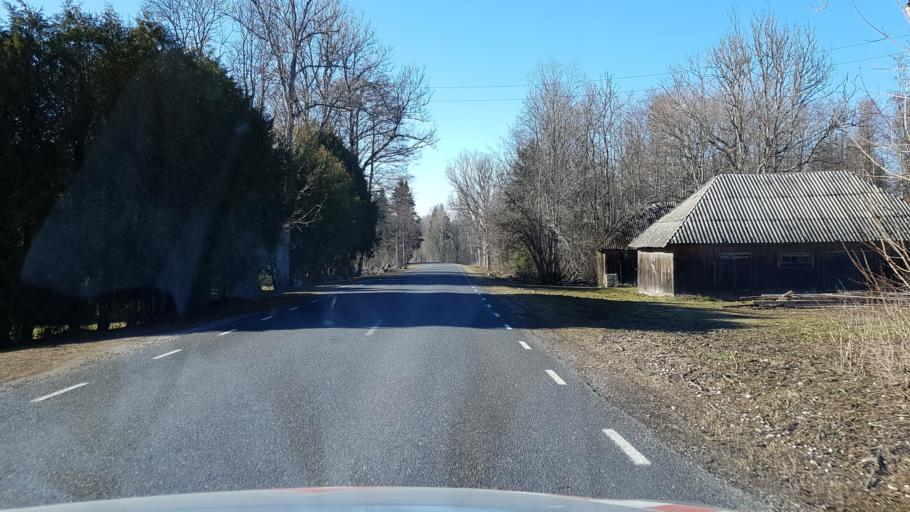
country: EE
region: Laeaene-Virumaa
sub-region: Kadrina vald
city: Kadrina
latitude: 59.5205
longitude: 26.0860
